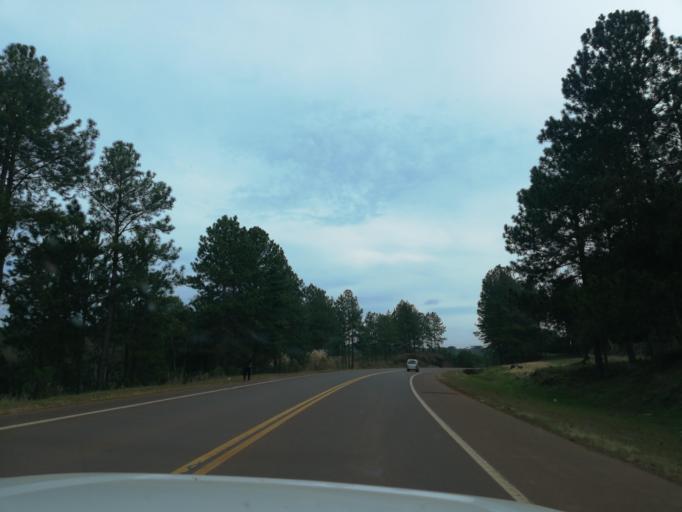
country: AR
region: Misiones
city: San Vicente
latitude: -26.6348
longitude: -54.1265
